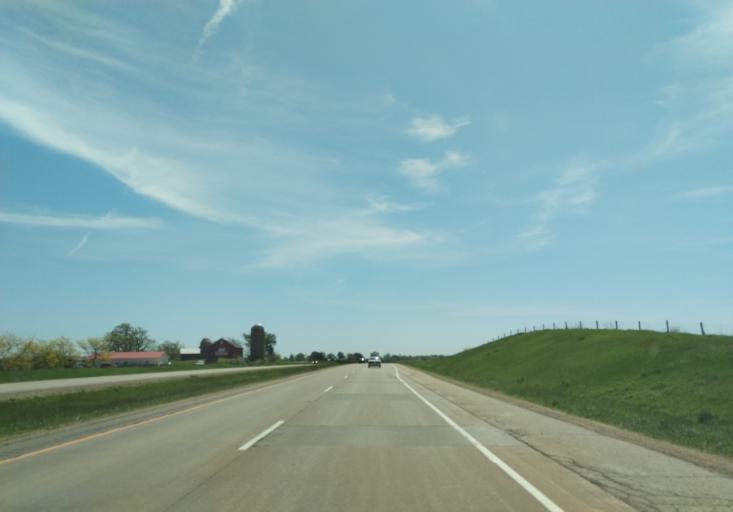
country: US
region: Wisconsin
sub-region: Dane County
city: Mount Horeb
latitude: 43.0016
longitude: -89.6760
